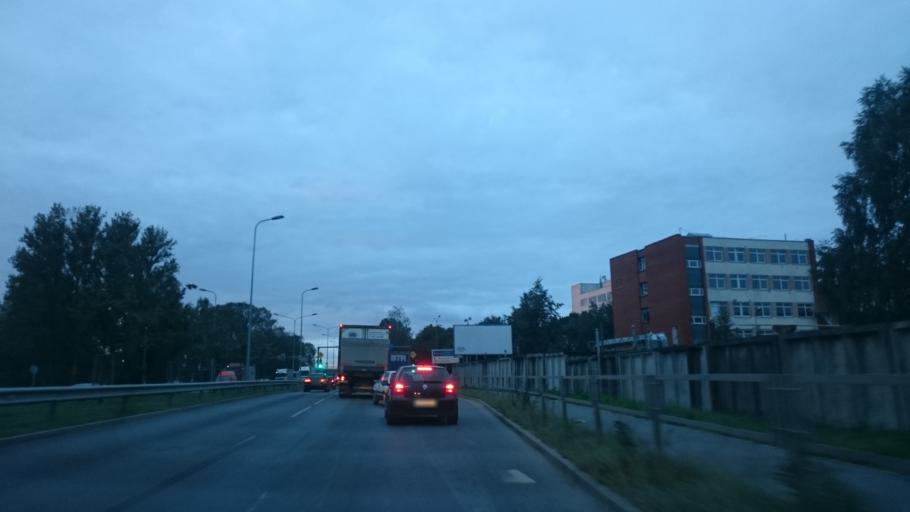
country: LV
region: Riga
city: Riga
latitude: 56.9250
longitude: 24.1886
